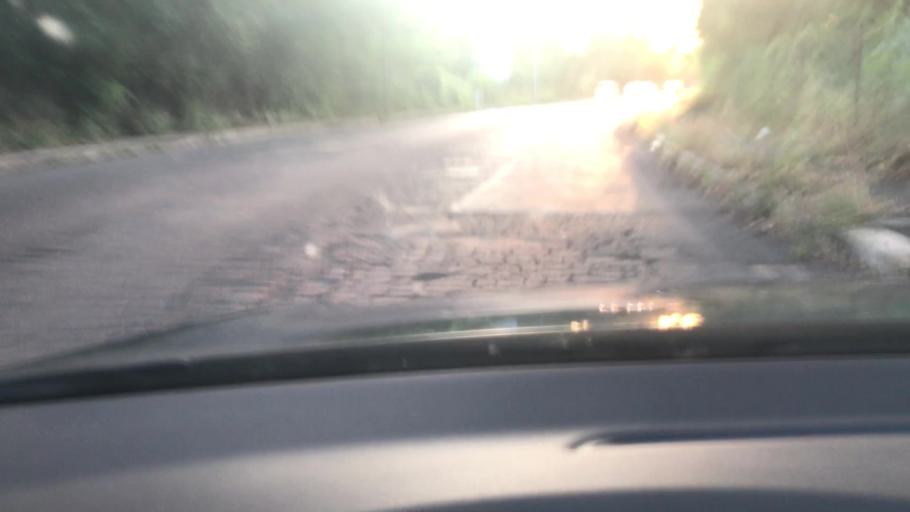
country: IT
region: Latium
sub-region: Citta metropolitana di Roma Capitale
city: Rome
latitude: 41.9244
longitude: 12.5668
